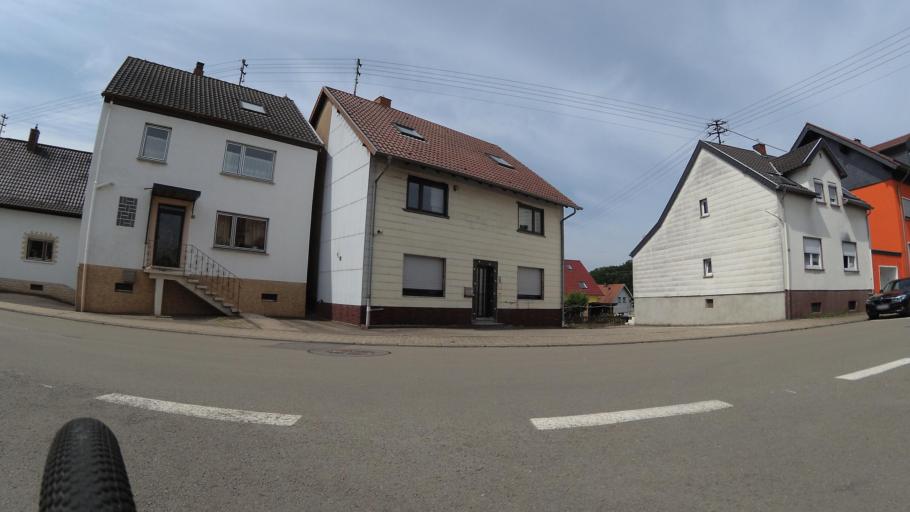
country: DE
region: Saarland
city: Merchweiler
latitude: 49.3346
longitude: 7.0562
